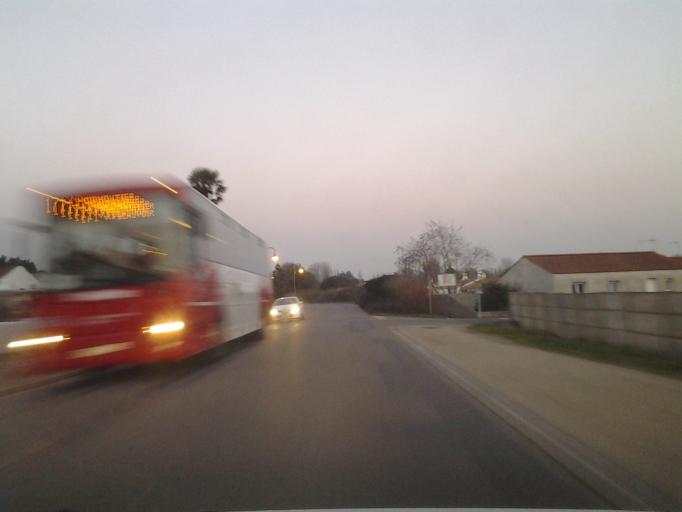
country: FR
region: Pays de la Loire
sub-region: Departement de la Vendee
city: Saint-Gervais
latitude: 46.9027
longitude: -2.0073
